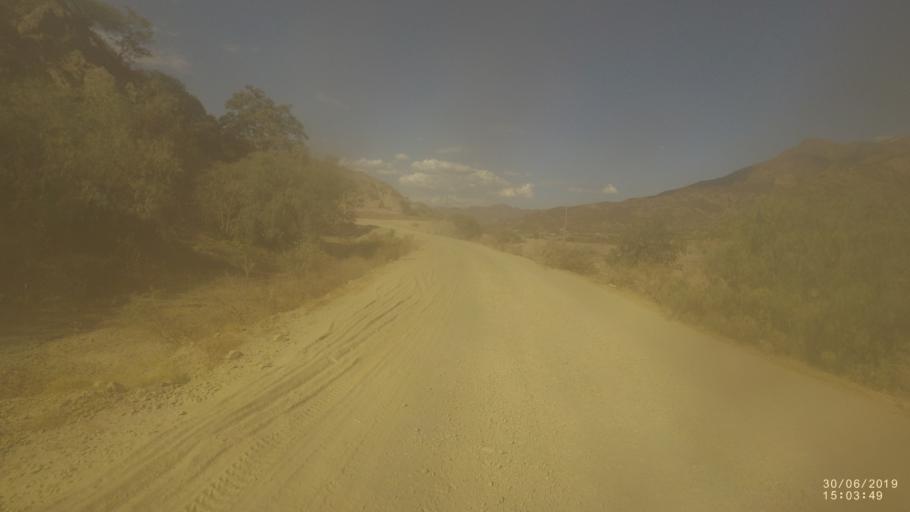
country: BO
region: Cochabamba
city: Irpa Irpa
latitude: -17.7316
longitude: -66.3246
